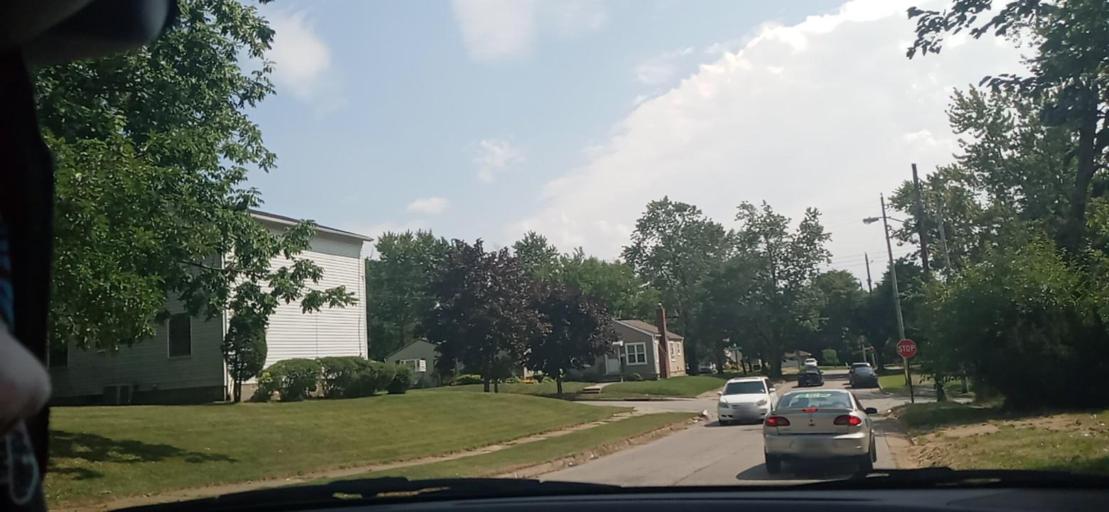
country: US
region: Ohio
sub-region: Summit County
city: Akron
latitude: 41.0619
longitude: -81.5610
